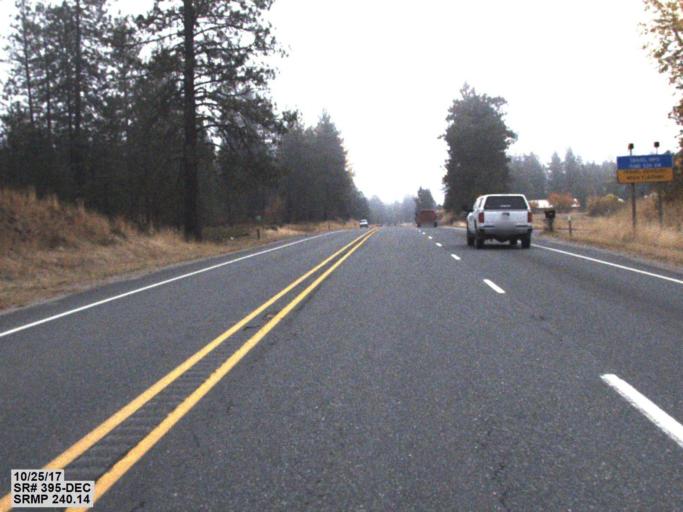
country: US
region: Washington
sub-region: Stevens County
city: Kettle Falls
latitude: 48.6118
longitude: -118.0943
